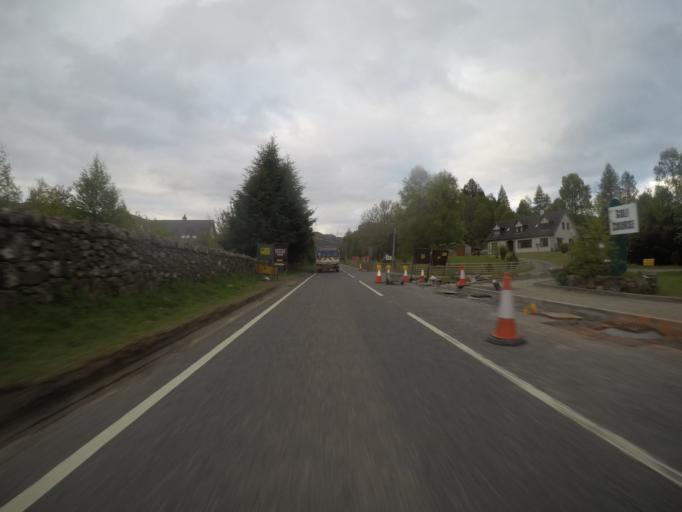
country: GB
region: Scotland
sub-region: Highland
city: Spean Bridge
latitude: 57.1350
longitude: -4.6890
